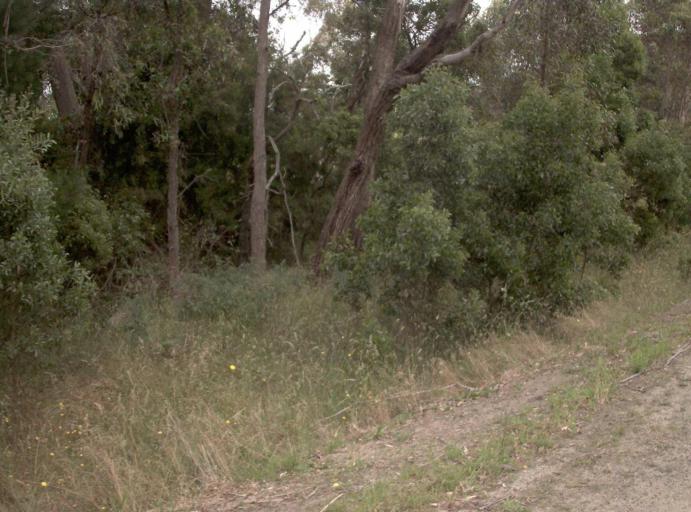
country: AU
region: Victoria
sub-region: Wellington
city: Sale
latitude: -38.5283
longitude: 146.8667
